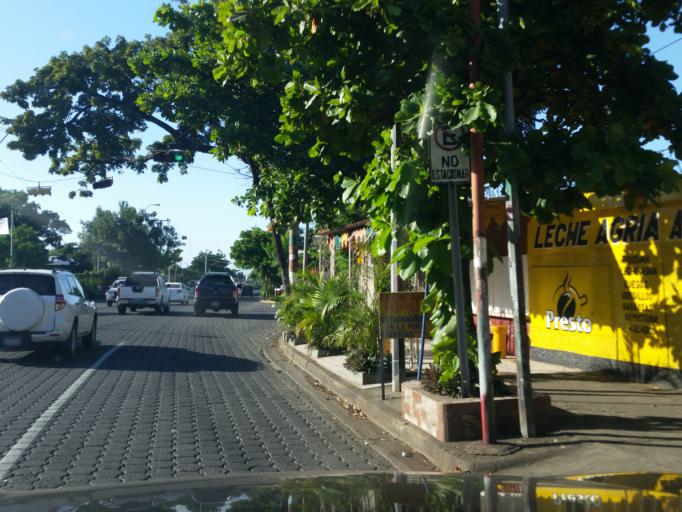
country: NI
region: Managua
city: Managua
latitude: 12.1387
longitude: -86.2930
